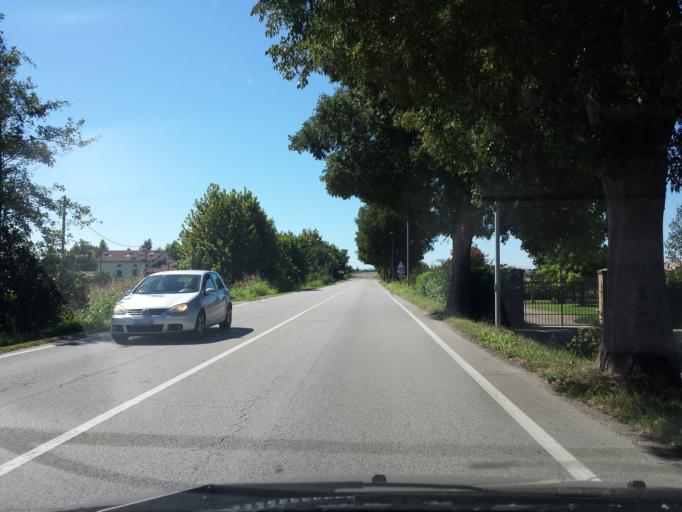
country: IT
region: Veneto
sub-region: Provincia di Vicenza
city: Dueville
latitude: 45.6194
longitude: 11.5679
